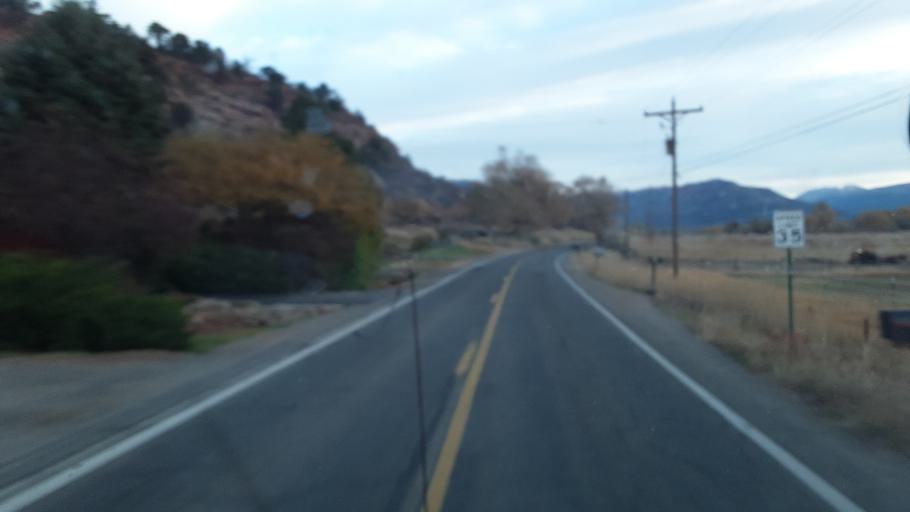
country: US
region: Colorado
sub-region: La Plata County
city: Durango
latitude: 37.3383
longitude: -107.8553
